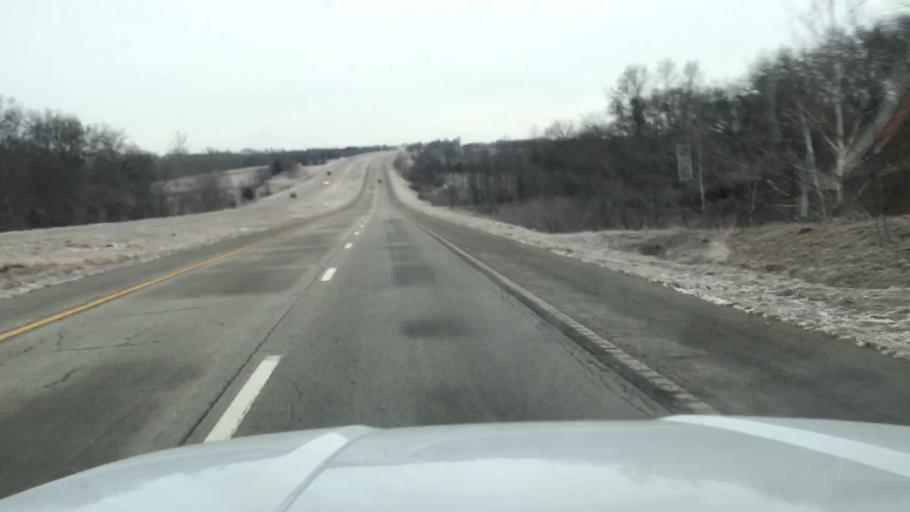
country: US
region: Missouri
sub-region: Andrew County
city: Savannah
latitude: 39.9046
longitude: -94.8580
